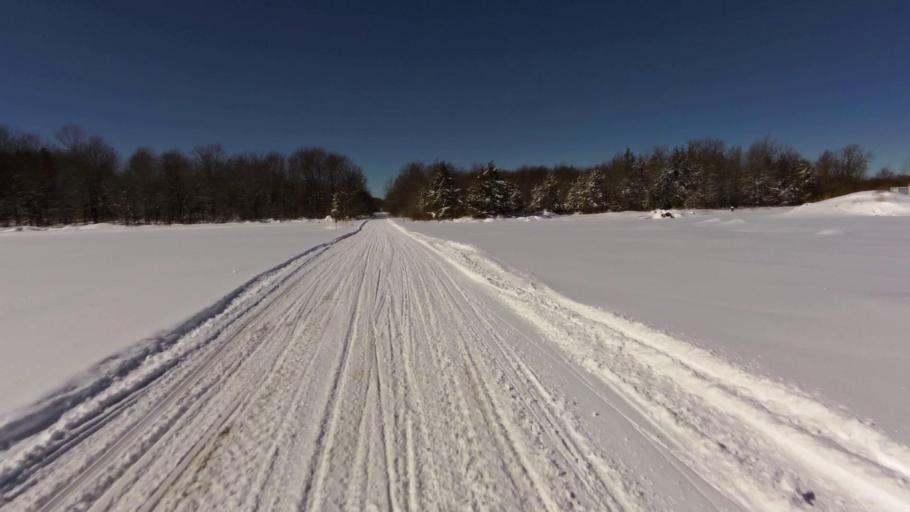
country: US
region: New York
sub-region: Chautauqua County
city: Lakewood
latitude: 42.2321
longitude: -79.3616
